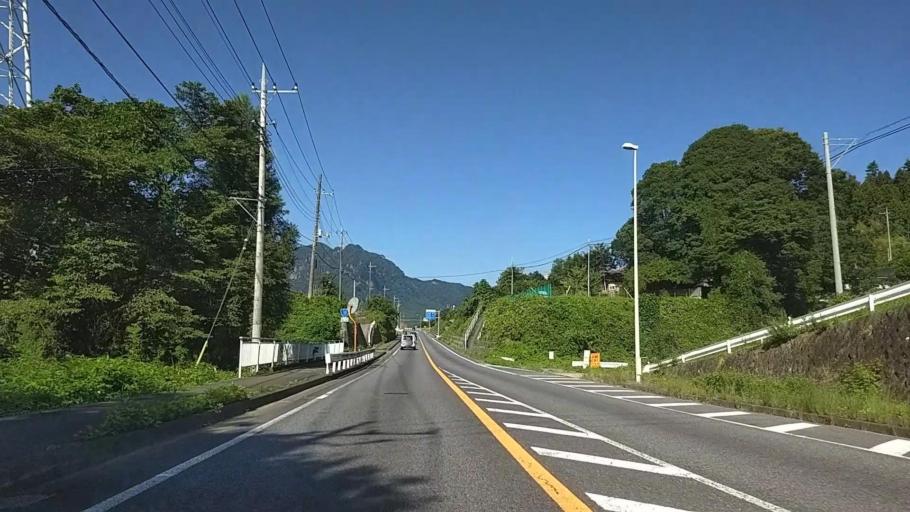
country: JP
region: Gunma
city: Annaka
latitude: 36.3205
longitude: 138.7815
